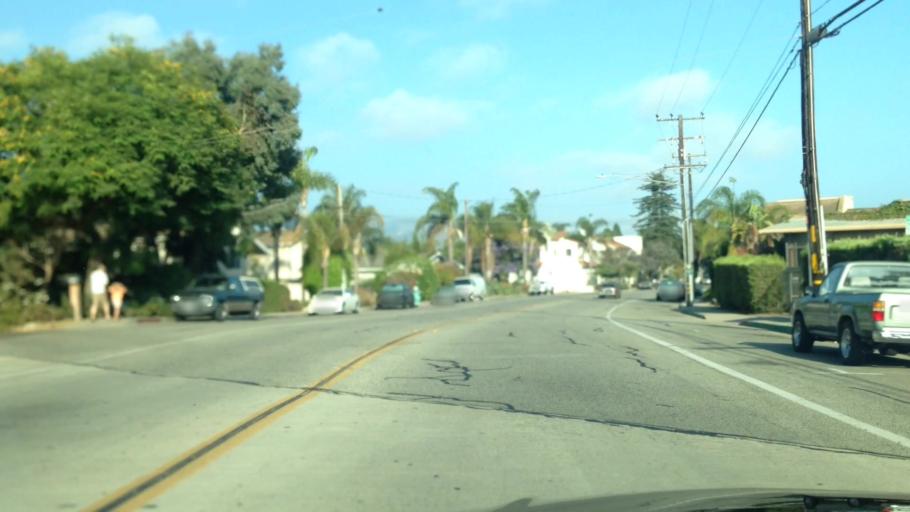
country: US
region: California
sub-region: Santa Barbara County
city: Carpinteria
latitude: 34.4013
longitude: -119.5217
